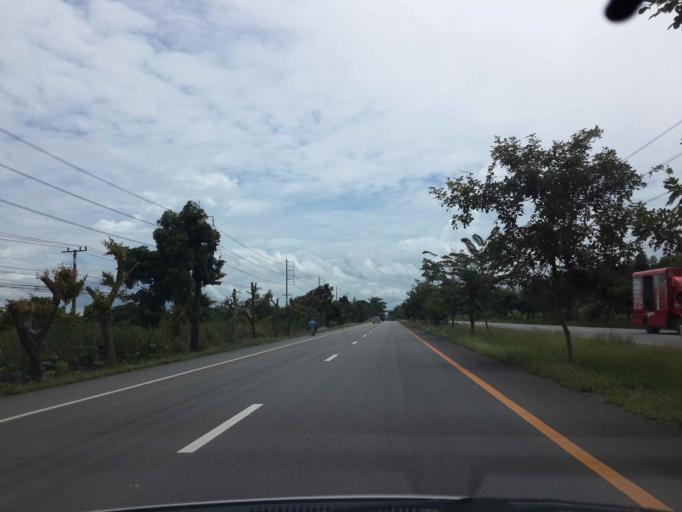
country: TH
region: Ratchaburi
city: Pak Tho
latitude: 13.4167
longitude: 99.8101
